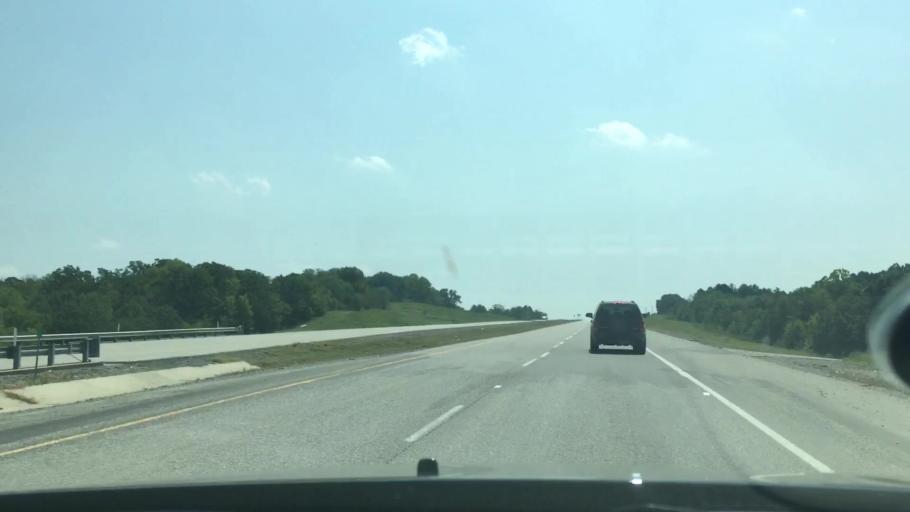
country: US
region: Oklahoma
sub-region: Atoka County
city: Atoka
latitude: 34.3529
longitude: -96.0862
